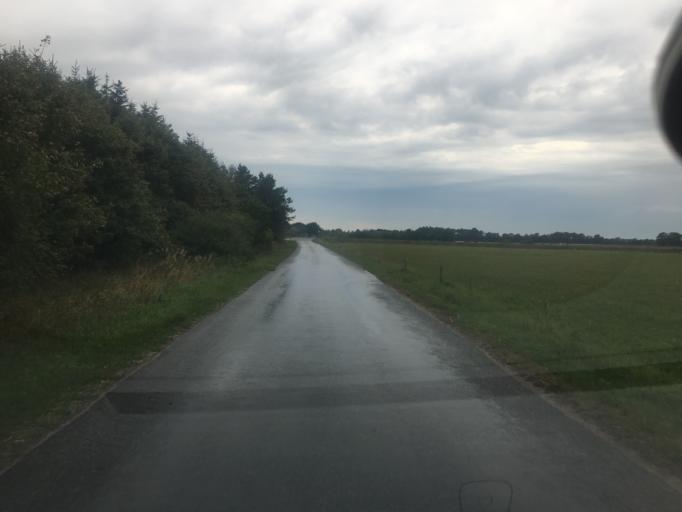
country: DK
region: South Denmark
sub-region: Tonder Kommune
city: Logumkloster
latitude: 55.0233
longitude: 8.9005
